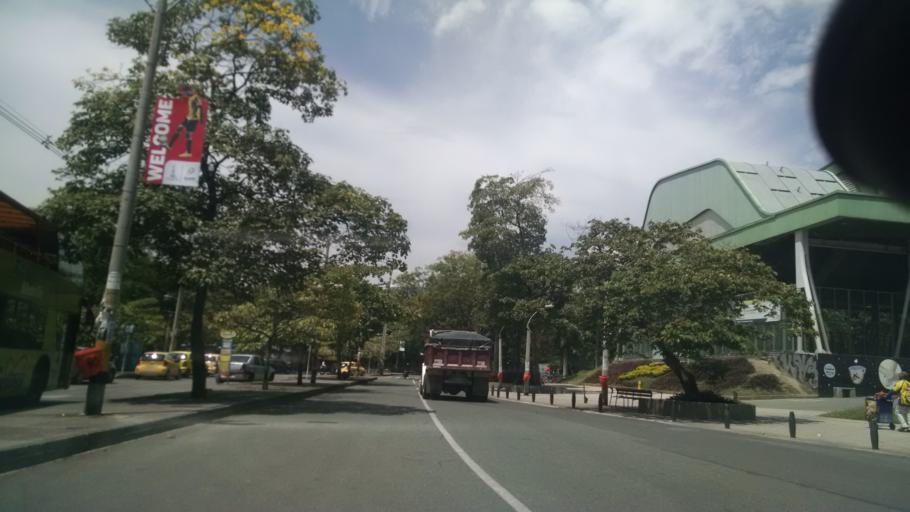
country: CO
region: Antioquia
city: Medellin
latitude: 6.2541
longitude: -75.5883
